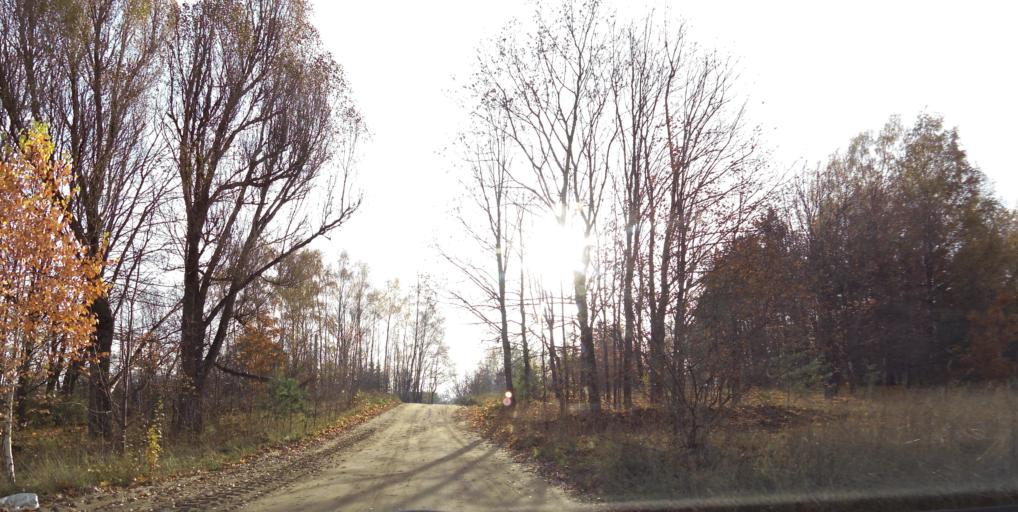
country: LT
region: Vilnius County
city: Pilaite
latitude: 54.7204
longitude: 25.1940
